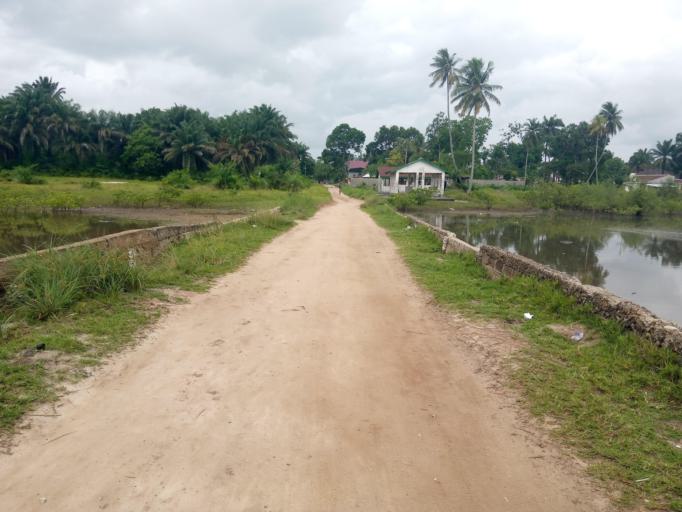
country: SL
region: Southern Province
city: Bonthe
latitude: 7.5275
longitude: -12.5030
